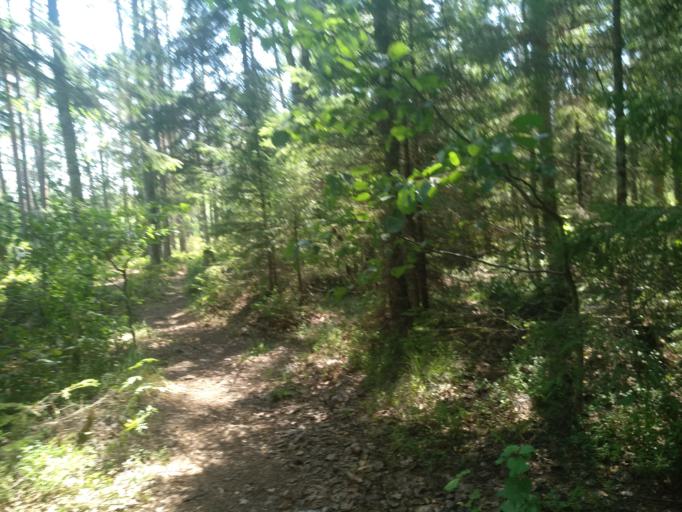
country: EE
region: Harju
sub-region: Kuusalu vald
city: Kuusalu
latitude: 59.2948
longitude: 25.6710
